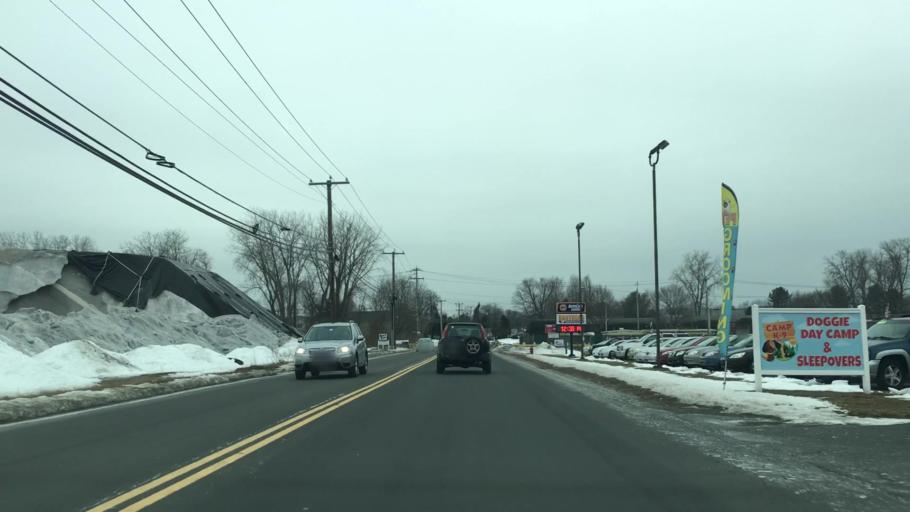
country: US
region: Massachusetts
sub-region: Hampden County
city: Westfield
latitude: 42.1269
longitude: -72.7271
